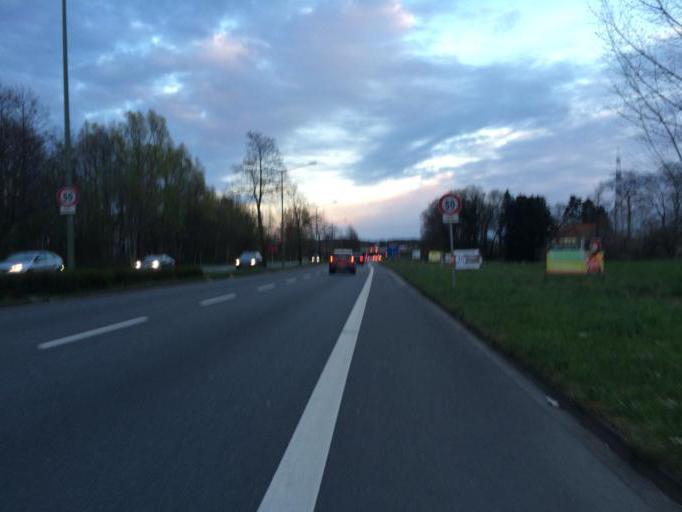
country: DE
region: Lower Saxony
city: Osnabrueck
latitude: 52.2580
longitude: 8.0863
